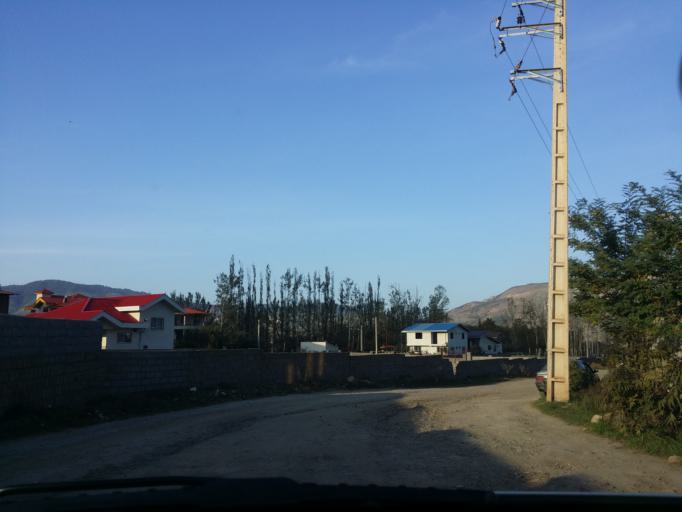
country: IR
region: Mazandaran
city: `Abbasabad
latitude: 36.5102
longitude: 51.1878
